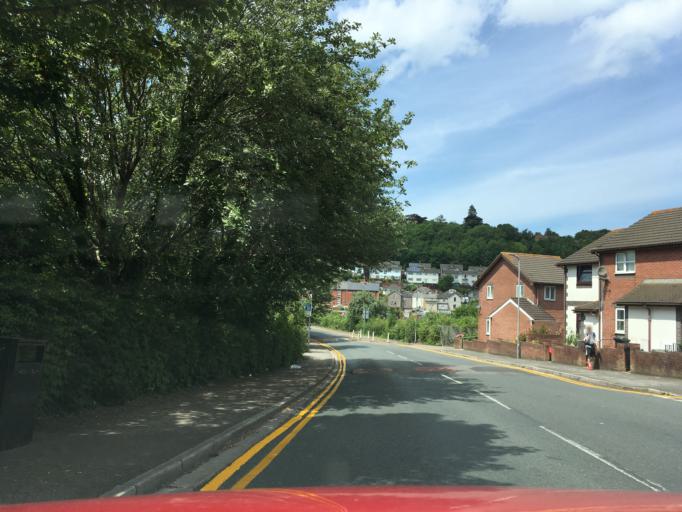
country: GB
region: Wales
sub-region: Newport
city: Caerleon
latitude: 51.5873
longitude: -2.9557
